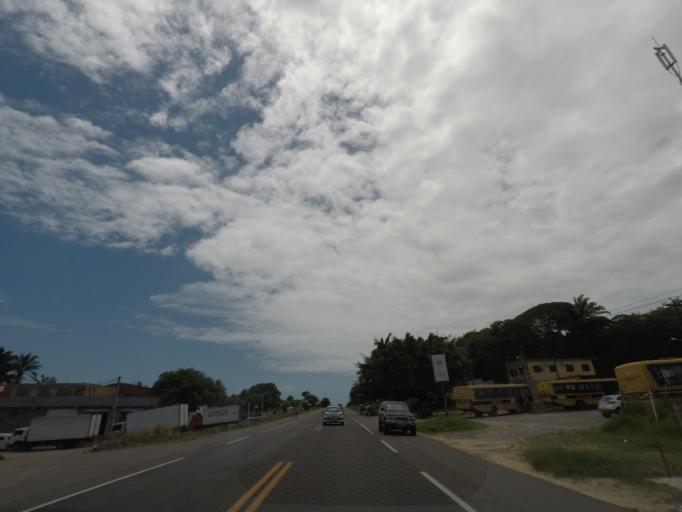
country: BR
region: Bahia
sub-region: Itaparica
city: Itaparica
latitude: -12.9545
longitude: -38.6323
